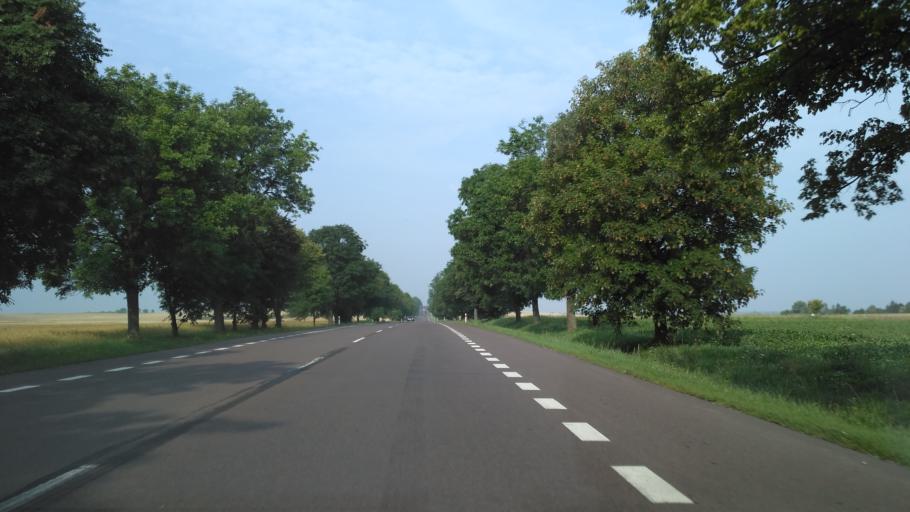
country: PL
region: Lublin Voivodeship
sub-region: Powiat leczynski
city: Cycow
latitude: 51.1718
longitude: 23.1286
